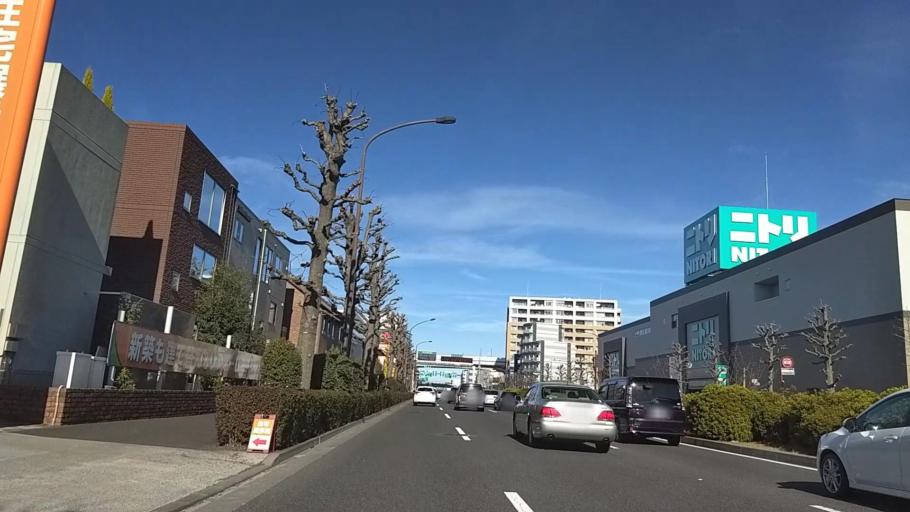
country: JP
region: Tokyo
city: Chofugaoka
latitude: 35.6244
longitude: 139.6273
